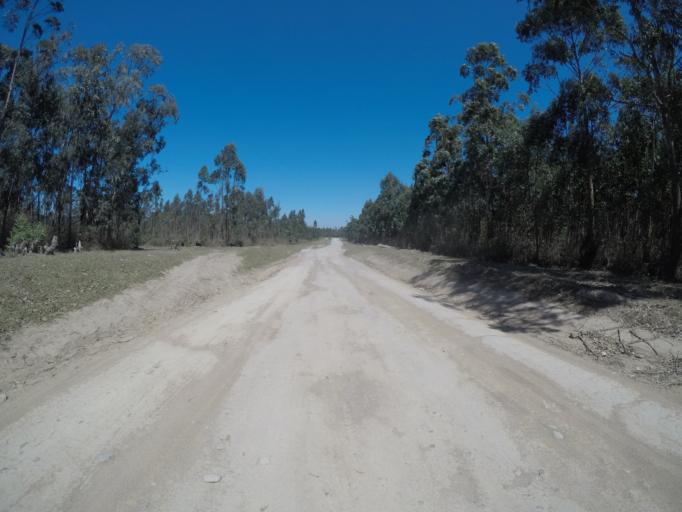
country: ZA
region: Eastern Cape
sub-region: OR Tambo District Municipality
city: Libode
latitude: -31.9501
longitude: 29.0247
